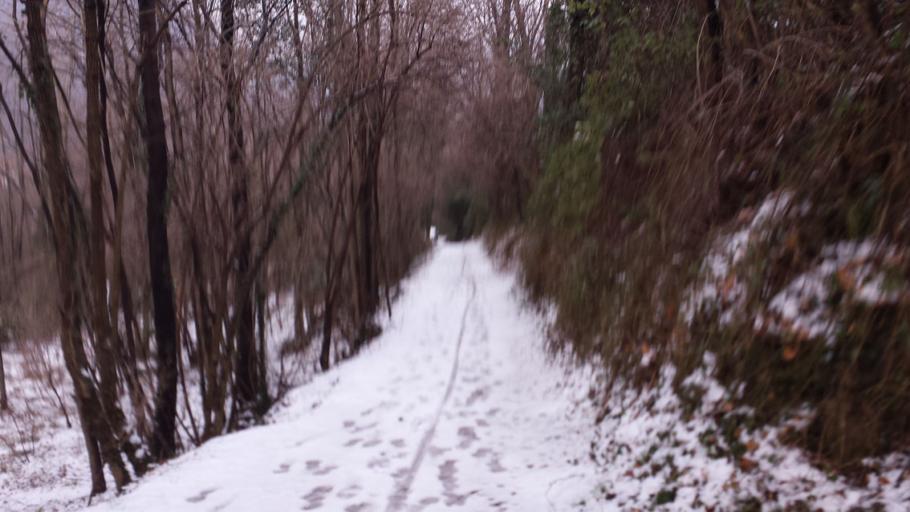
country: IT
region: Veneto
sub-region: Provincia di Vicenza
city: Campese
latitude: 45.7998
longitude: 11.7151
